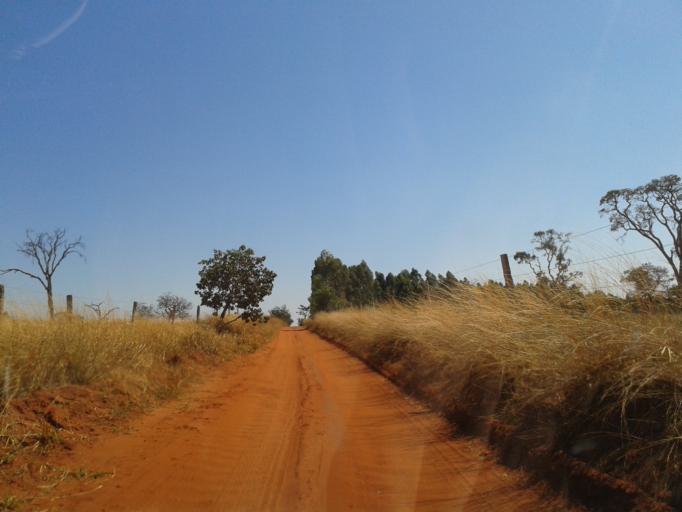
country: BR
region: Minas Gerais
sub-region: Ituiutaba
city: Ituiutaba
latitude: -19.0219
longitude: -49.2159
